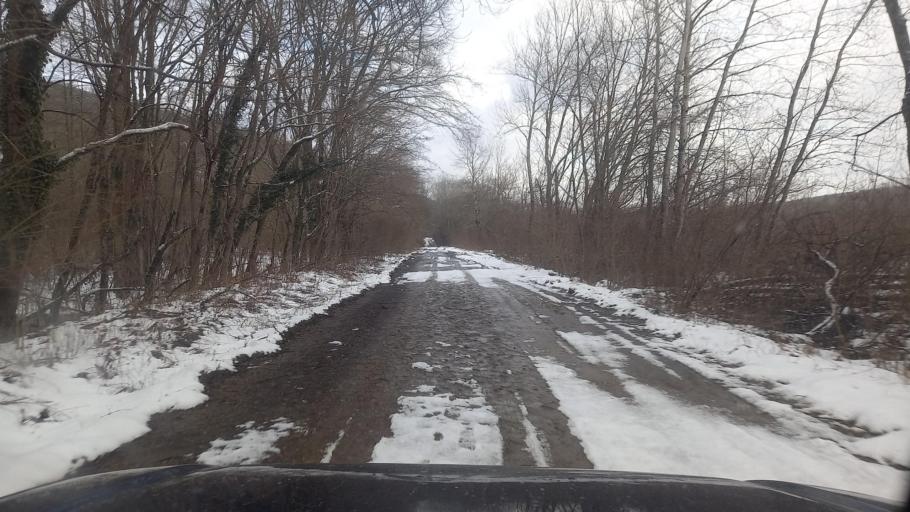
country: RU
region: Krasnodarskiy
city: Smolenskaya
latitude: 44.6899
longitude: 38.8575
